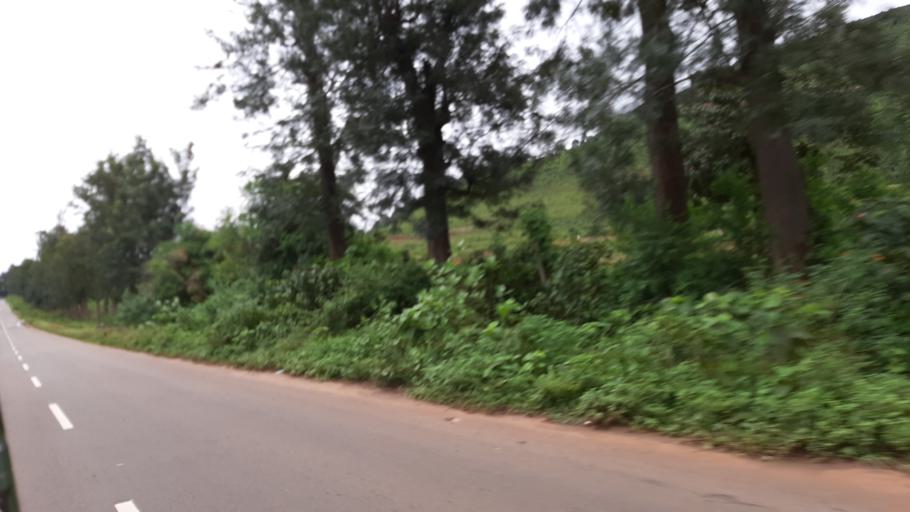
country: IN
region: Andhra Pradesh
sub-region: Vizianagaram District
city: Salur
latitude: 18.2937
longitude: 82.9179
